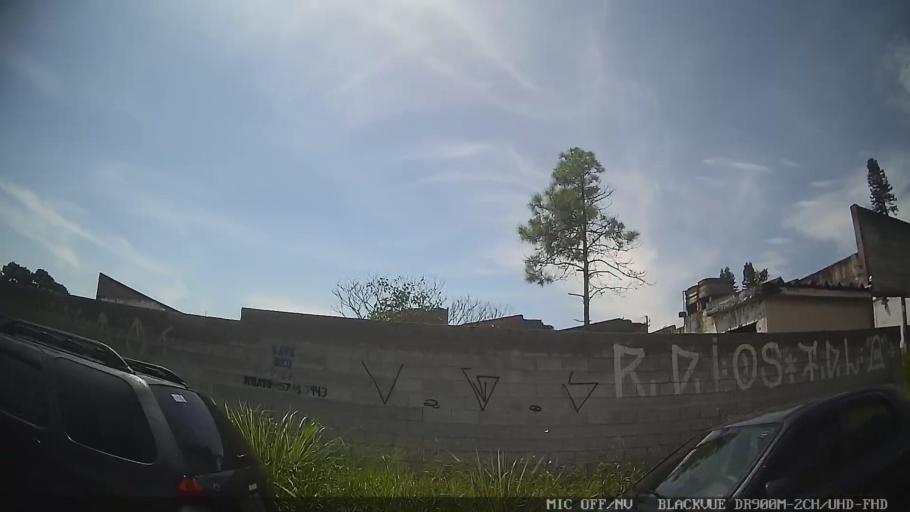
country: BR
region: Sao Paulo
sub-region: Poa
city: Poa
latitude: -23.5145
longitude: -46.3337
